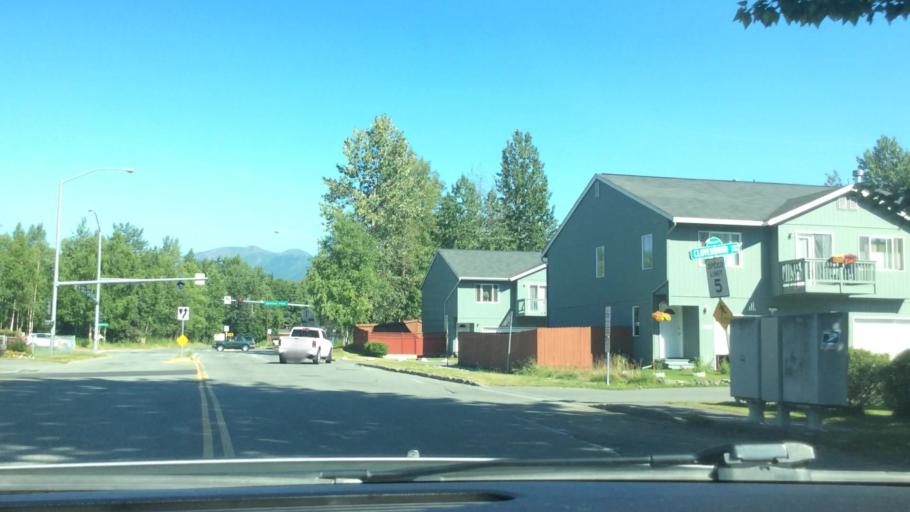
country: US
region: Alaska
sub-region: Anchorage Municipality
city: Anchorage
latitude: 61.1989
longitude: -149.7801
